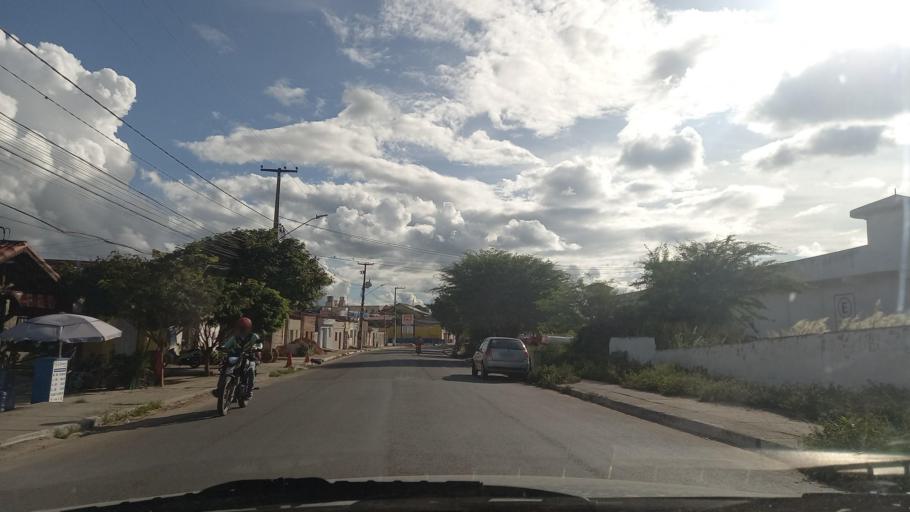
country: BR
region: Pernambuco
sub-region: Gravata
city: Gravata
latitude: -8.2061
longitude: -35.5808
